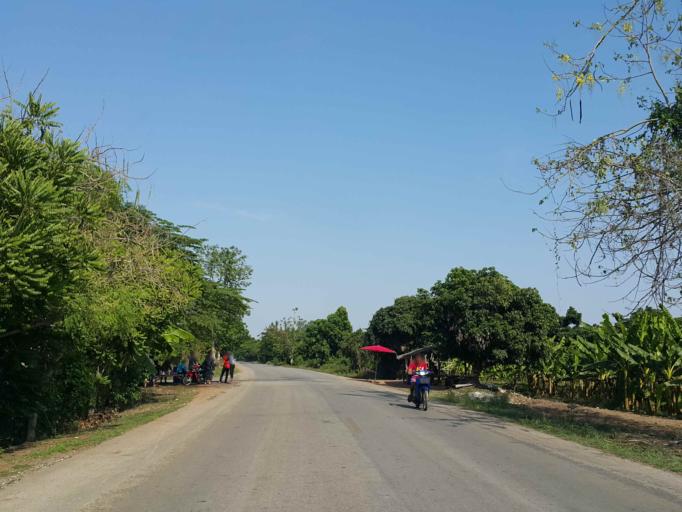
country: TH
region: Sukhothai
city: Thung Saliam
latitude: 17.3281
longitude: 99.6160
